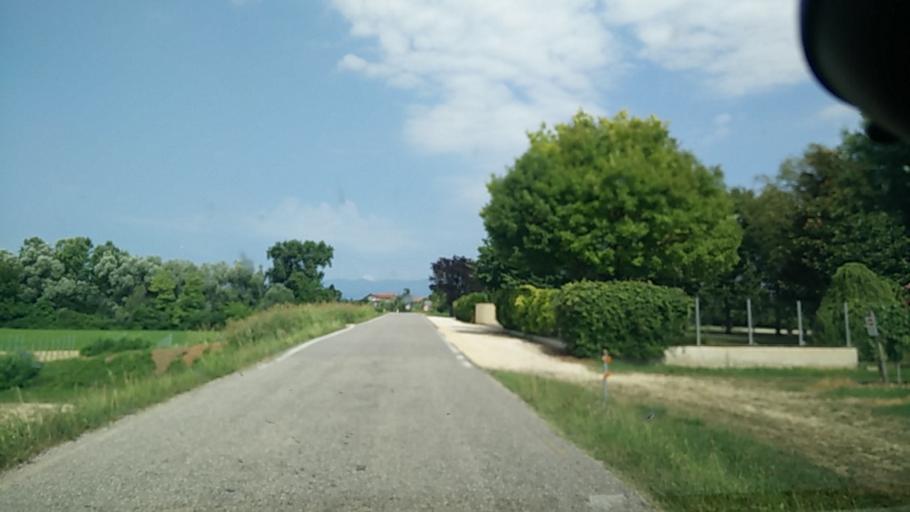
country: IT
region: Veneto
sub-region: Provincia di Treviso
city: Portobuffole
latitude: 45.8515
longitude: 12.5532
